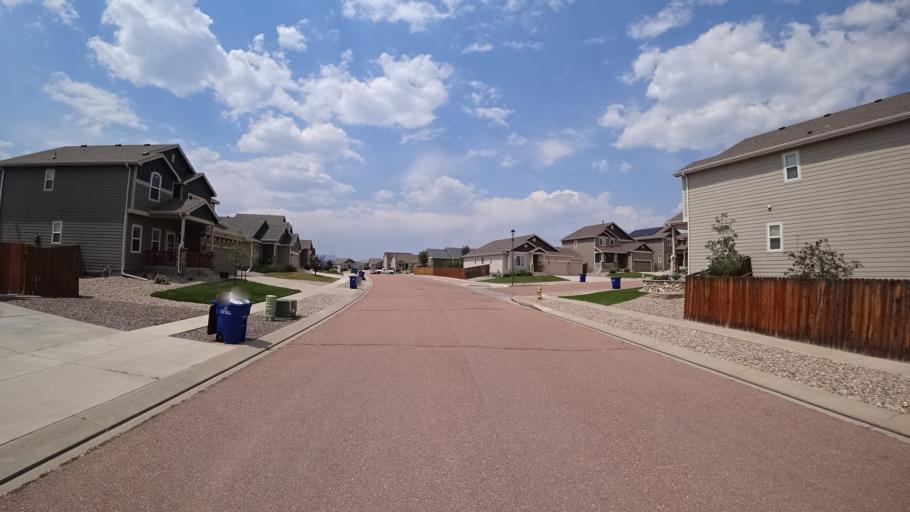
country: US
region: Colorado
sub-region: El Paso County
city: Black Forest
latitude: 38.9518
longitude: -104.6978
